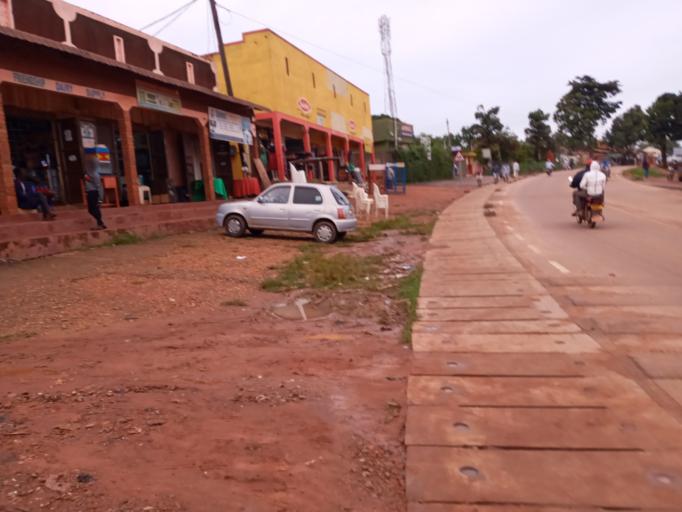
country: UG
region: Central Region
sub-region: Wakiso District
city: Bweyogerere
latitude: 0.3347
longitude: 32.6707
